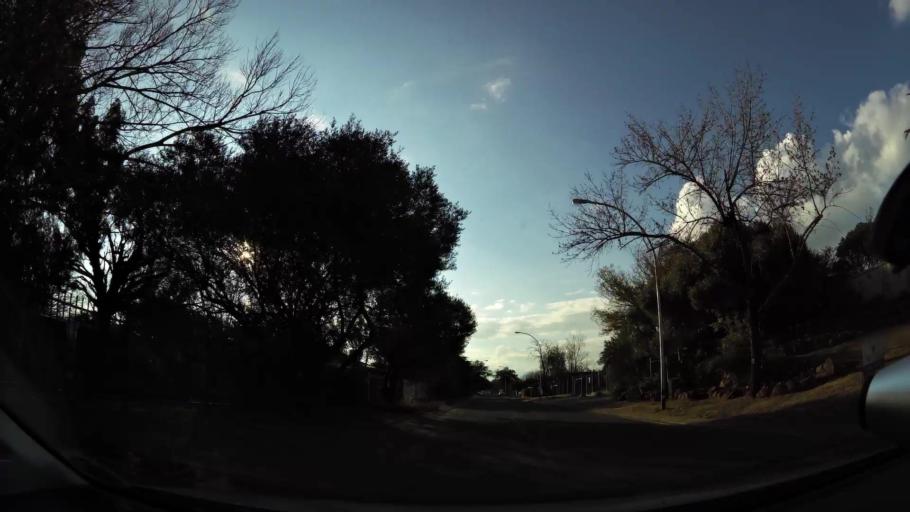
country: ZA
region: Orange Free State
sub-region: Mangaung Metropolitan Municipality
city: Bloemfontein
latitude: -29.1533
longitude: 26.1760
